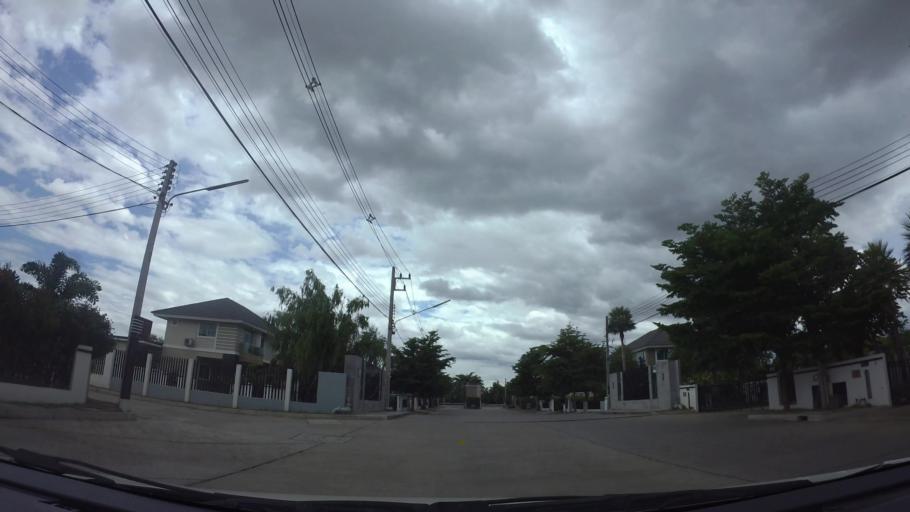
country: TH
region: Chiang Mai
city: Saraphi
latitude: 18.7475
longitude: 99.0424
